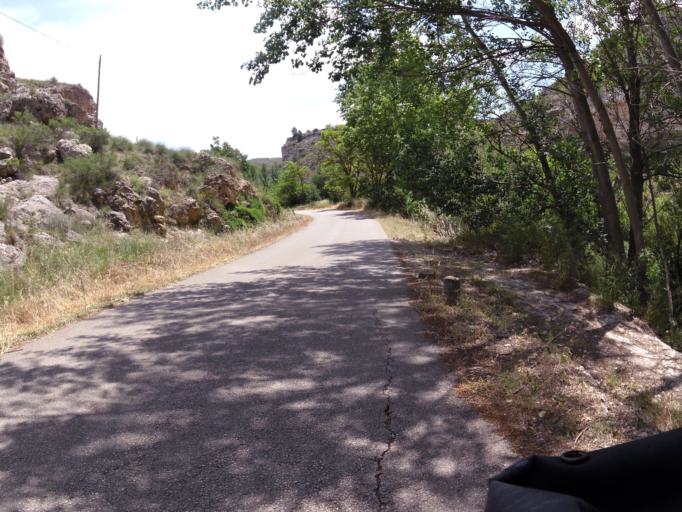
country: ES
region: Castille-La Mancha
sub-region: Provincia de Albacete
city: Casas de Juan Nunez
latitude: 39.1588
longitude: -1.5953
